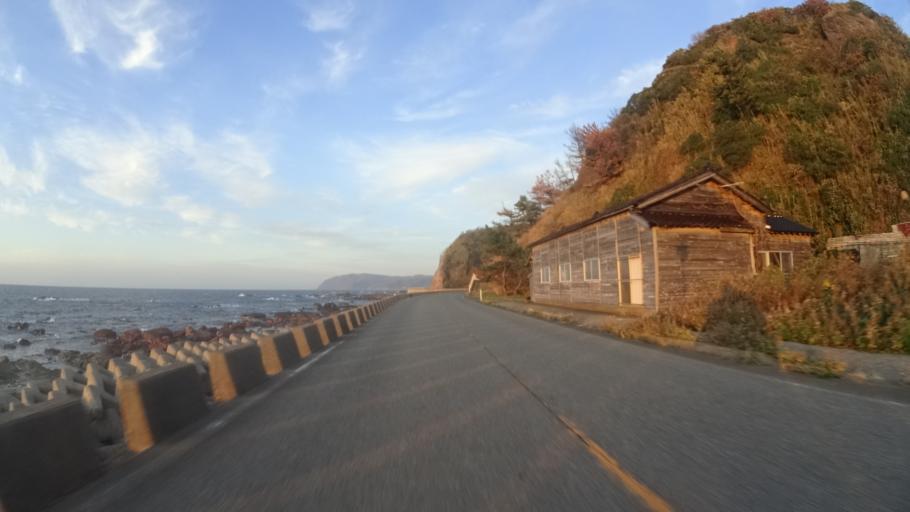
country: JP
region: Ishikawa
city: Nanao
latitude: 37.2424
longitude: 136.7020
